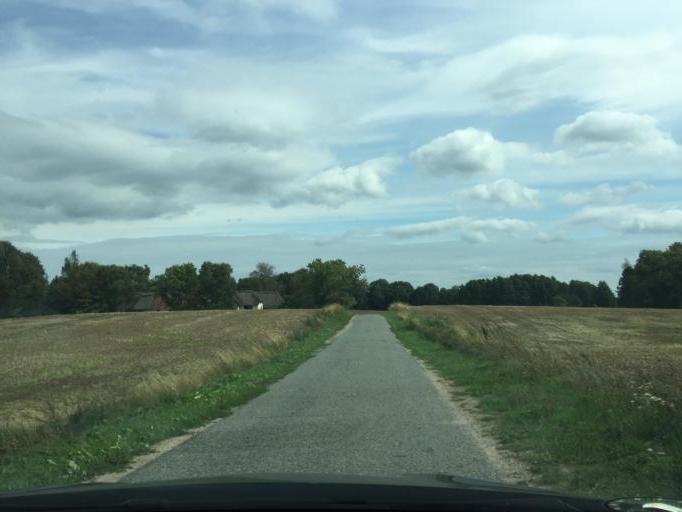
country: DK
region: South Denmark
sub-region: Nordfyns Kommune
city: Sonderso
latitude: 55.4142
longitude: 10.2189
